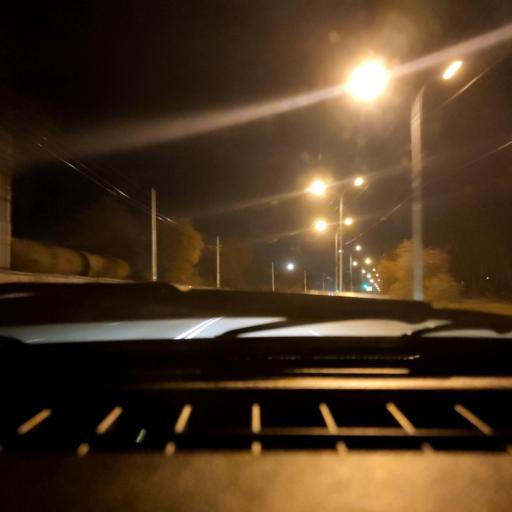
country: RU
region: Bashkortostan
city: Ufa
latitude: 54.8307
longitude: 56.0883
